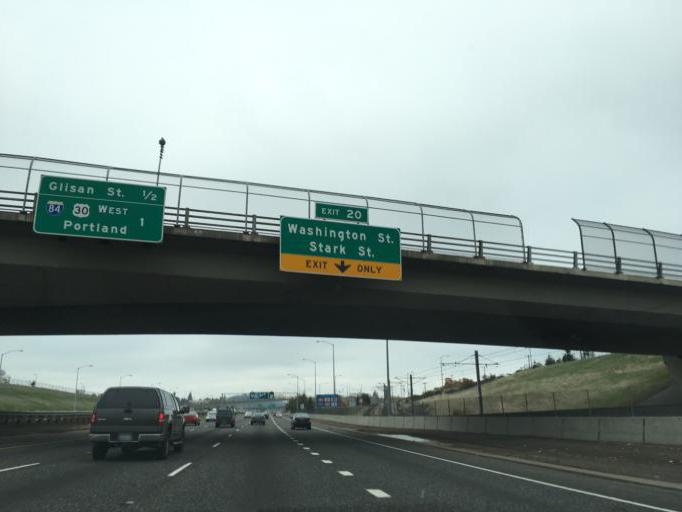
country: US
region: Oregon
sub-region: Multnomah County
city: Lents
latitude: 45.5104
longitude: -122.5653
